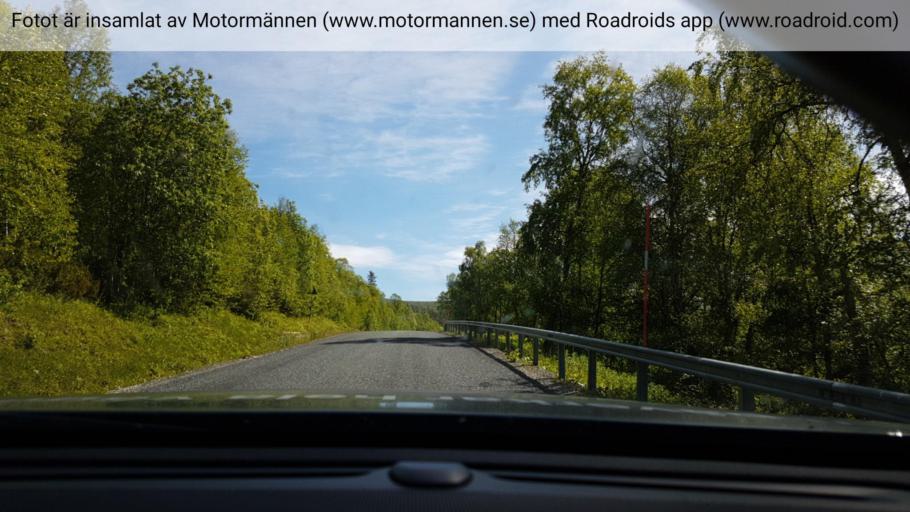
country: SE
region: Vaesterbotten
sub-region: Vilhelmina Kommun
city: Sjoberg
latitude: 65.3235
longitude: 15.2693
